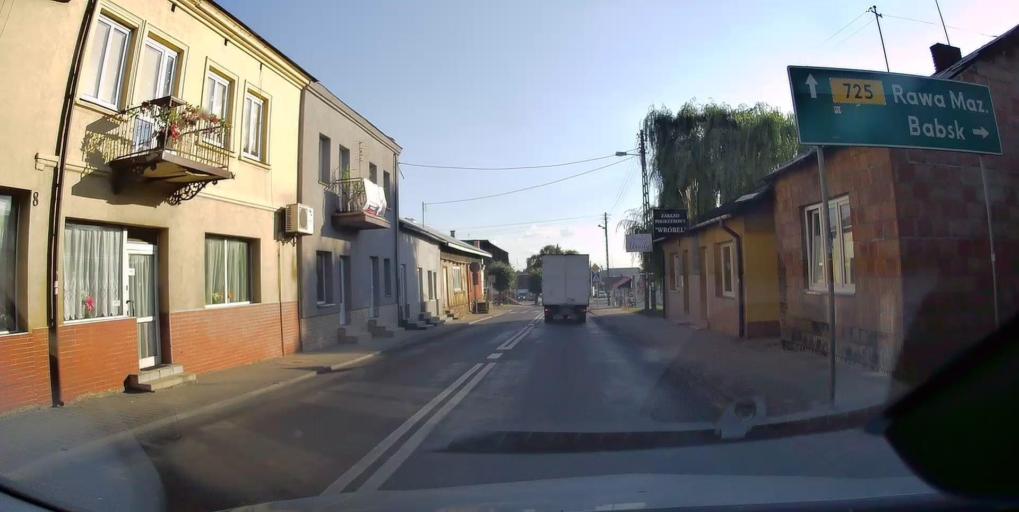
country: PL
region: Lodz Voivodeship
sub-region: Powiat rawski
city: Biala Rawska
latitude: 51.8085
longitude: 20.4737
